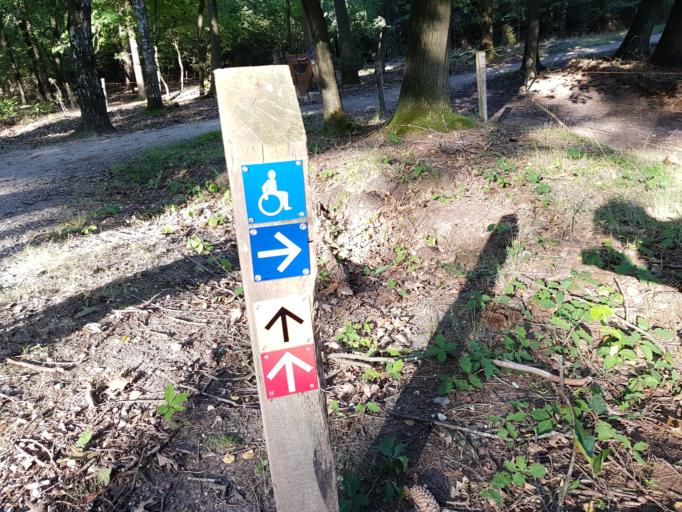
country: NL
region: Utrecht
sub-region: Gemeente Utrechtse Heuvelrug
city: Leersum
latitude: 52.0350
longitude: 5.4230
